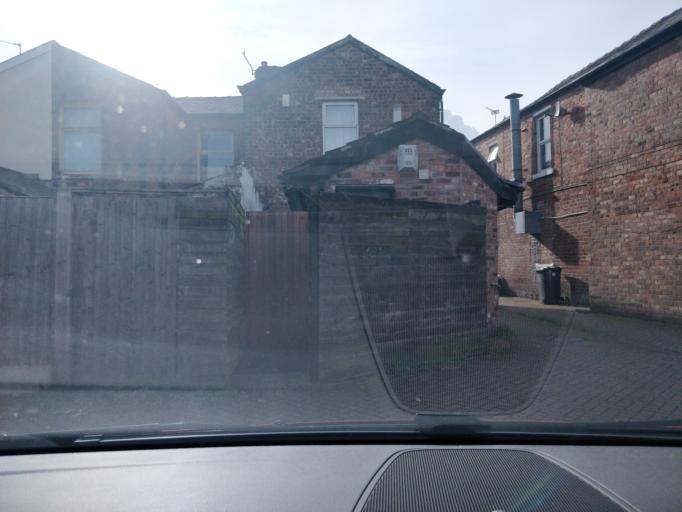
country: GB
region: England
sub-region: Sefton
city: Southport
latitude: 53.6369
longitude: -3.0088
